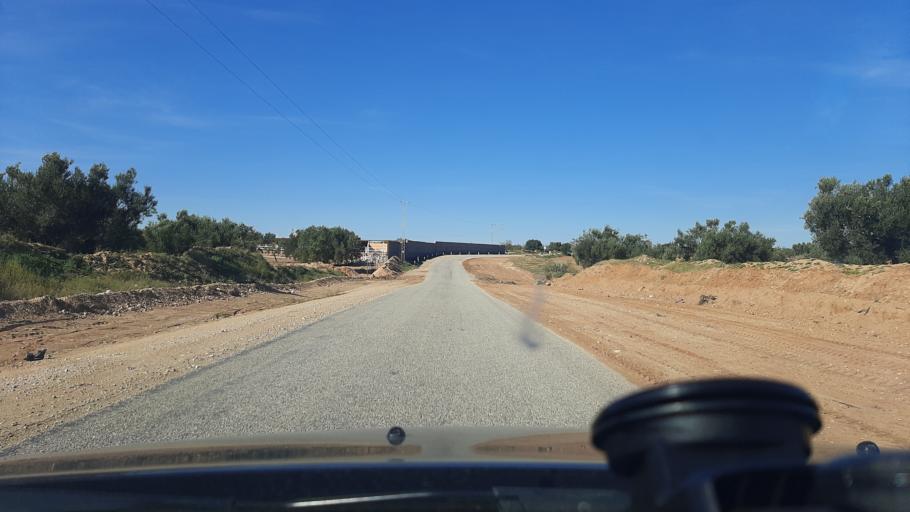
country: TN
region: Safaqis
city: Sfax
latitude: 34.9102
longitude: 10.5904
